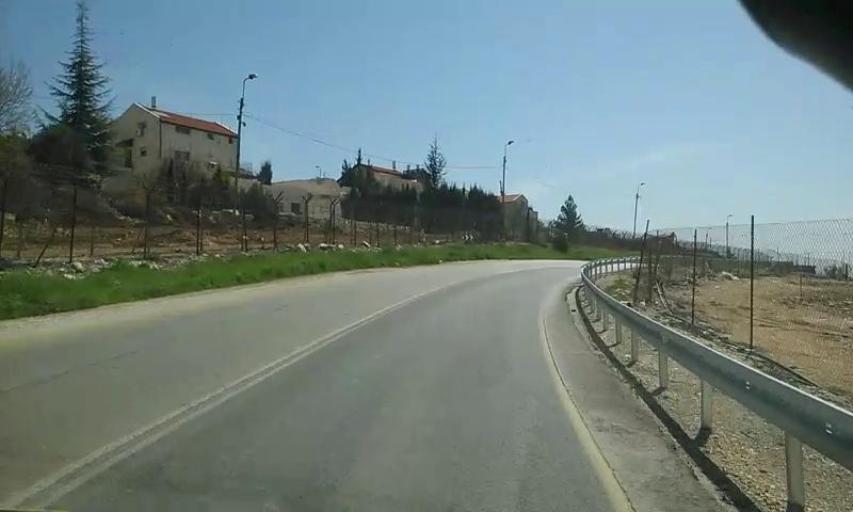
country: PS
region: West Bank
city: Nahhalin
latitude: 31.6532
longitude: 35.1252
